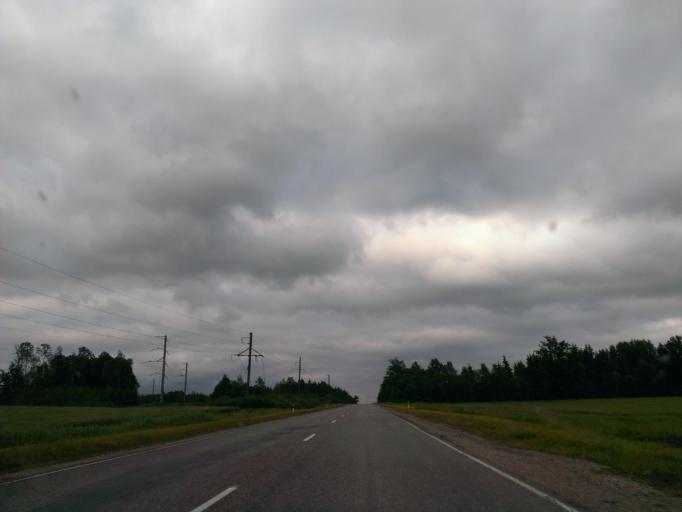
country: LV
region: Saldus Rajons
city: Saldus
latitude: 56.6710
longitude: 22.3917
